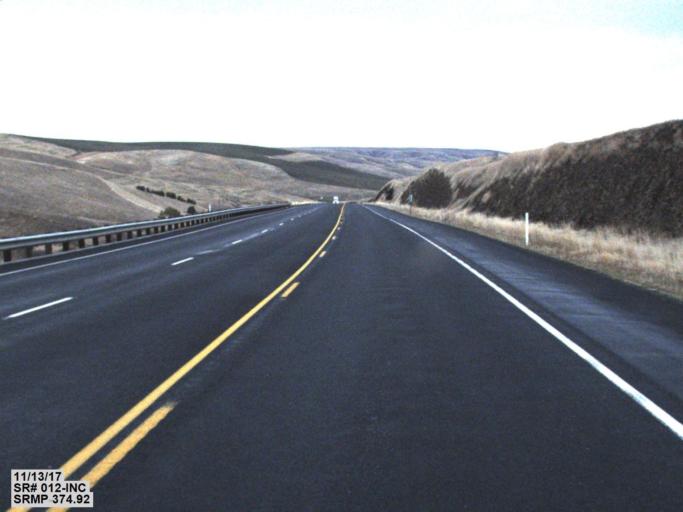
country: US
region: Washington
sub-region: Columbia County
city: Dayton
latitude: 46.4111
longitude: -117.9426
